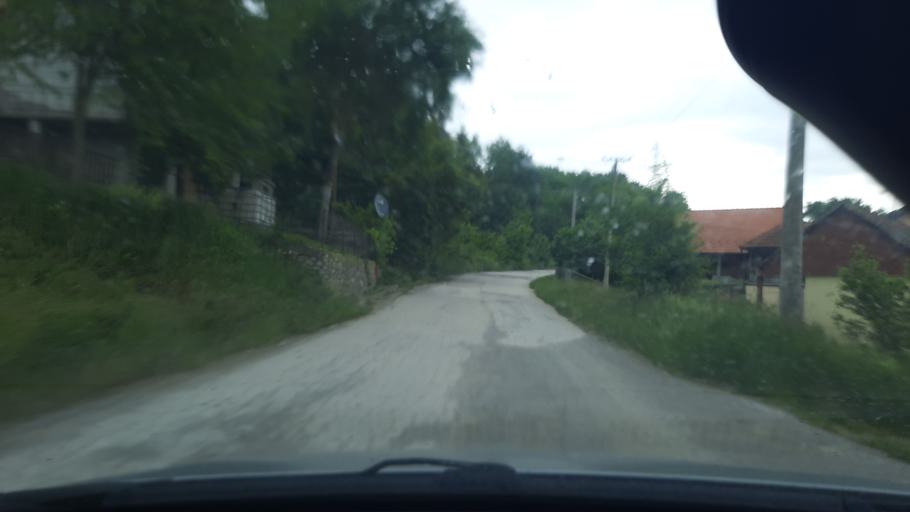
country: RS
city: Jarebice
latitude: 44.4839
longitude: 19.4764
